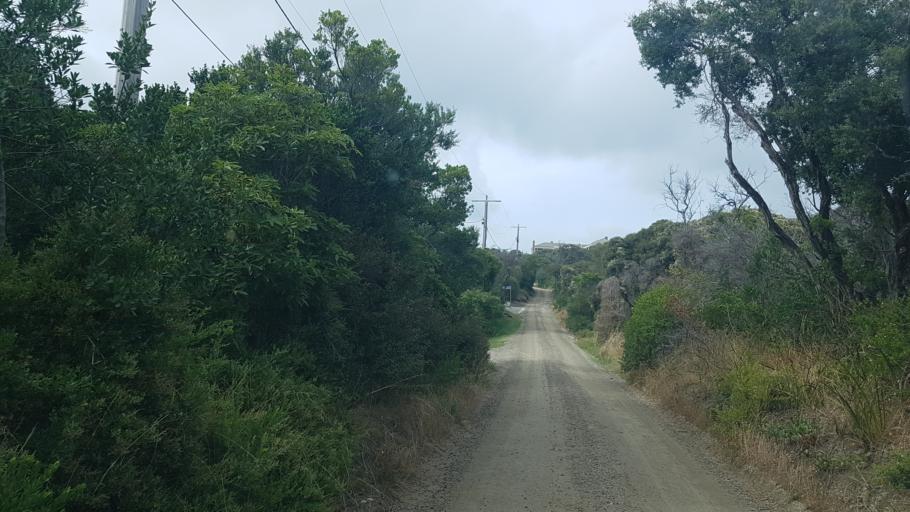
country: AU
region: Victoria
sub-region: Mornington Peninsula
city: Sorrento
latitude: -38.3280
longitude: 144.7049
